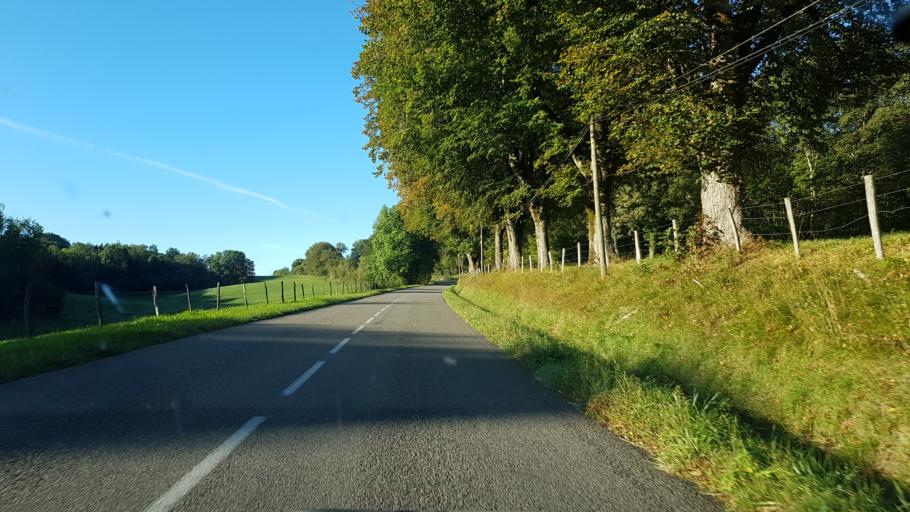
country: FR
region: Franche-Comte
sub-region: Departement du Jura
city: Lons-le-Saunier
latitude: 46.6342
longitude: 5.5372
